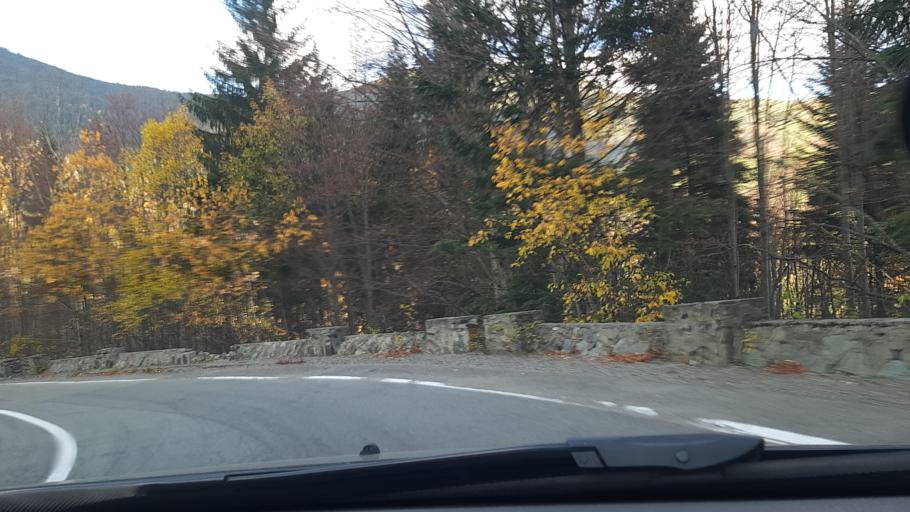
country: RO
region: Valcea
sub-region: Comuna Voineasa
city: Voineasa
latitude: 45.4329
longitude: 23.8610
